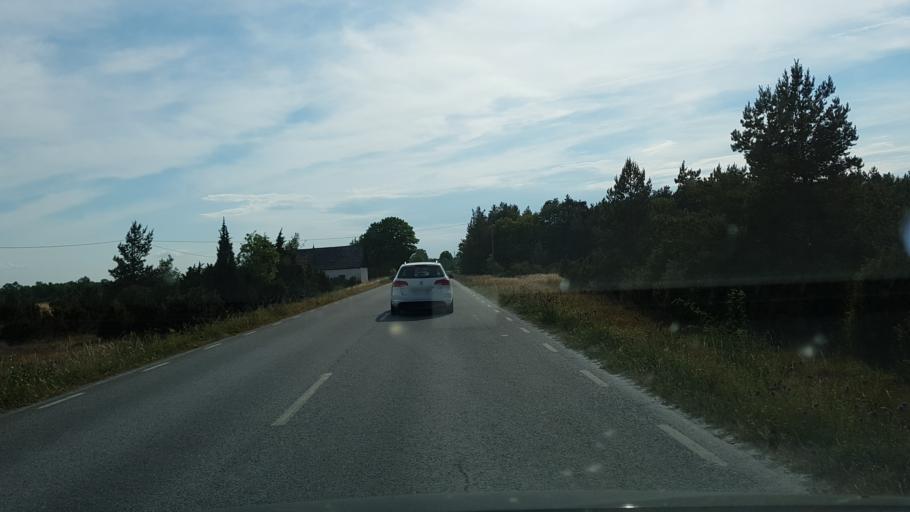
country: SE
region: Gotland
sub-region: Gotland
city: Visby
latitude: 57.6353
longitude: 18.4533
